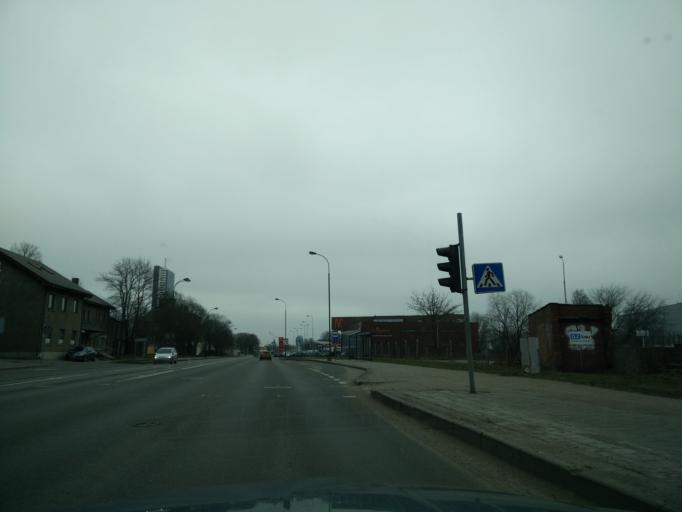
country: LT
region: Klaipedos apskritis
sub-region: Klaipeda
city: Klaipeda
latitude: 55.6962
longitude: 21.1385
